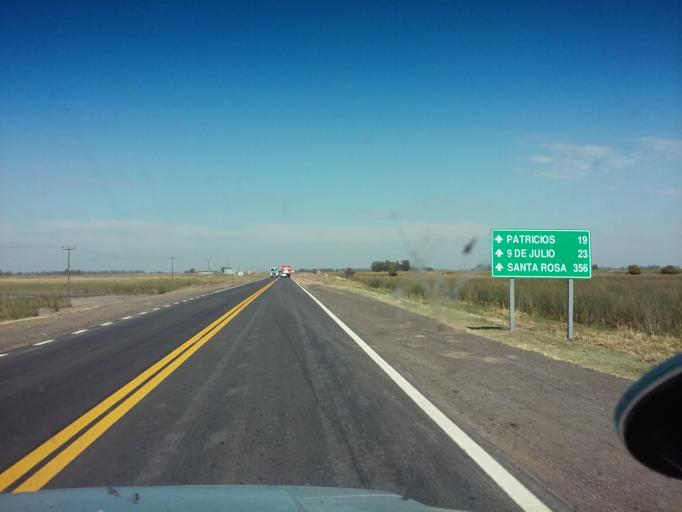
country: AR
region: Buenos Aires
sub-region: Partido de Nueve de Julio
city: Nueve de Julio
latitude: -35.3702
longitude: -60.7142
